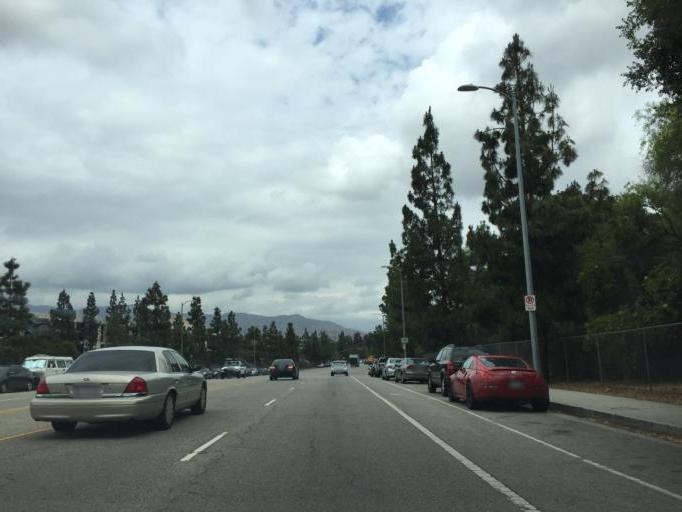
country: US
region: California
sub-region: Los Angeles County
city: Universal City
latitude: 34.1455
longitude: -118.3370
